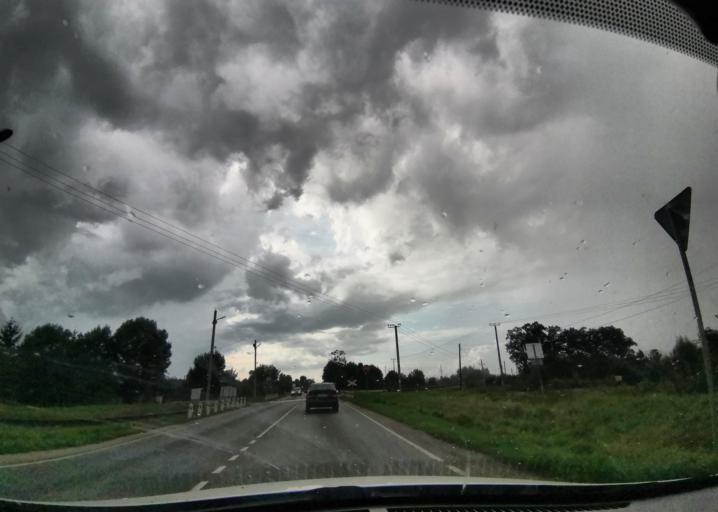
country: RU
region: Kaliningrad
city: Chernyakhovsk
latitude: 54.6264
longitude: 21.8575
